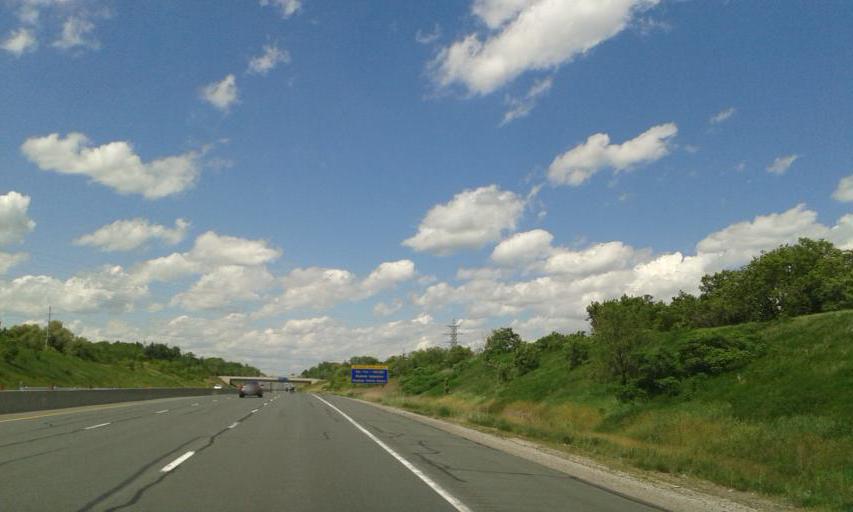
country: CA
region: Ontario
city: Burlington
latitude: 43.3525
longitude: -79.8313
